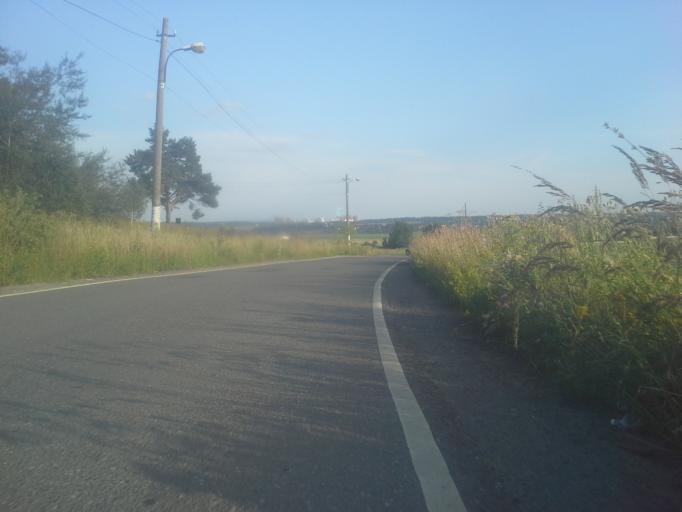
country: RU
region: Moskovskaya
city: Nikolina Gora
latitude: 55.7404
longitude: 36.9894
